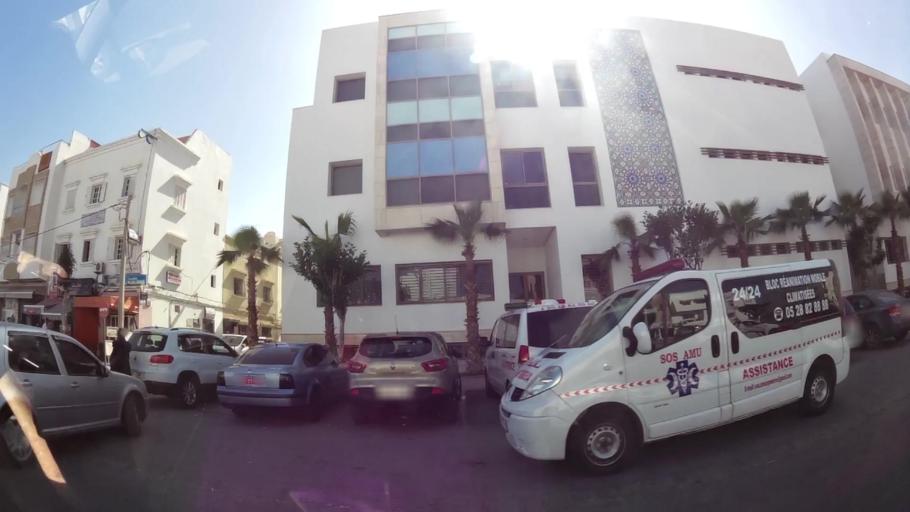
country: MA
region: Souss-Massa-Draa
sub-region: Agadir-Ida-ou-Tnan
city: Agadir
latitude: 30.4172
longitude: -9.5900
